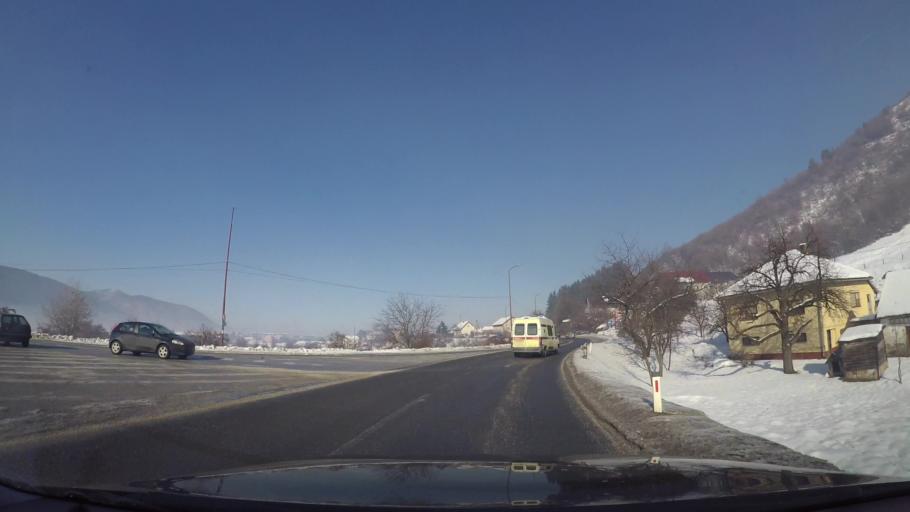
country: BA
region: Federation of Bosnia and Herzegovina
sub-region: Kanton Sarajevo
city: Sarajevo
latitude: 43.8021
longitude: 18.3493
